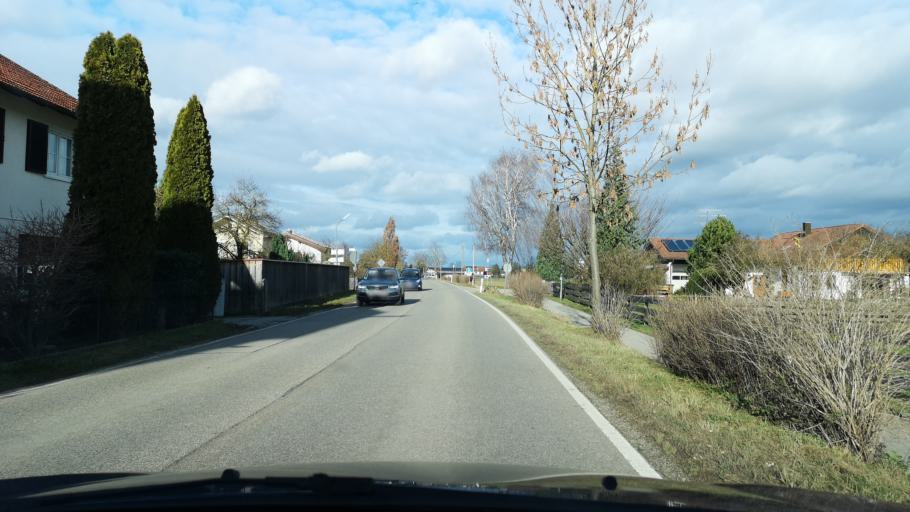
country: DE
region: Bavaria
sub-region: Upper Bavaria
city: Poing
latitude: 48.1581
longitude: 11.8169
